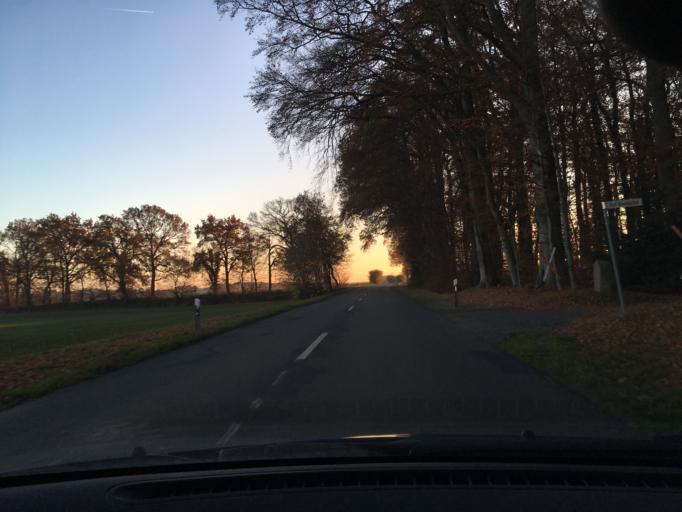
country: DE
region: Lower Saxony
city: Natendorf
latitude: 53.0759
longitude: 10.4628
